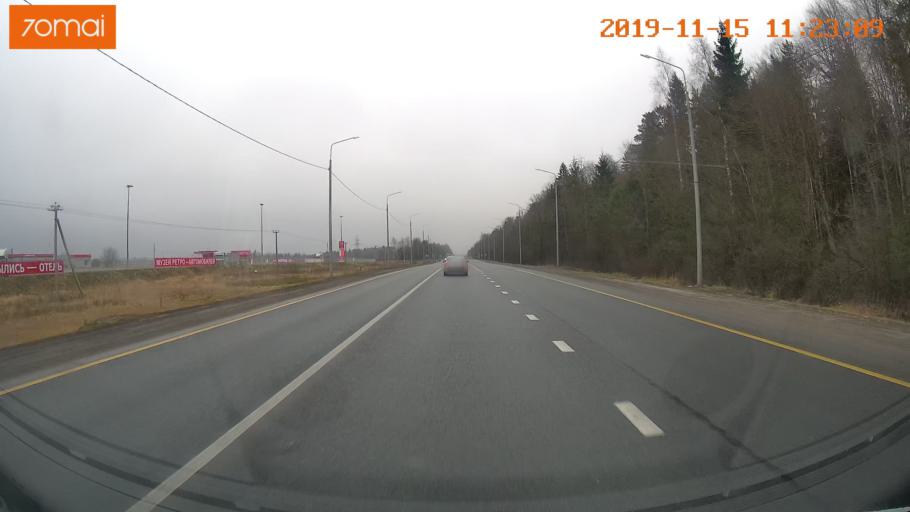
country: RU
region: Vologda
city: Molochnoye
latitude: 59.1498
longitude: 39.3754
